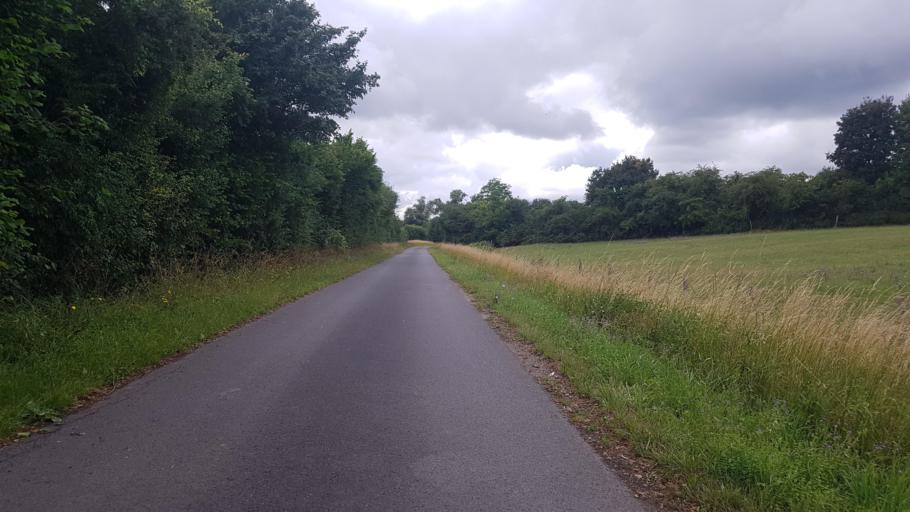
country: FR
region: Lorraine
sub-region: Departement de la Moselle
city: Lorquin
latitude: 48.7083
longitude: 7.0144
